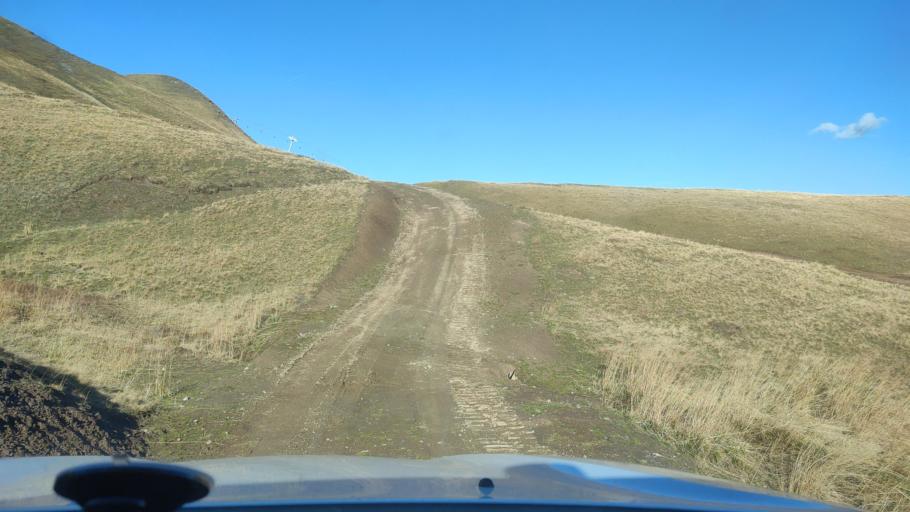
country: FR
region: Rhone-Alpes
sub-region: Departement de la Savoie
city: Saint-Etienne-de-Cuines
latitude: 45.2413
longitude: 6.2214
